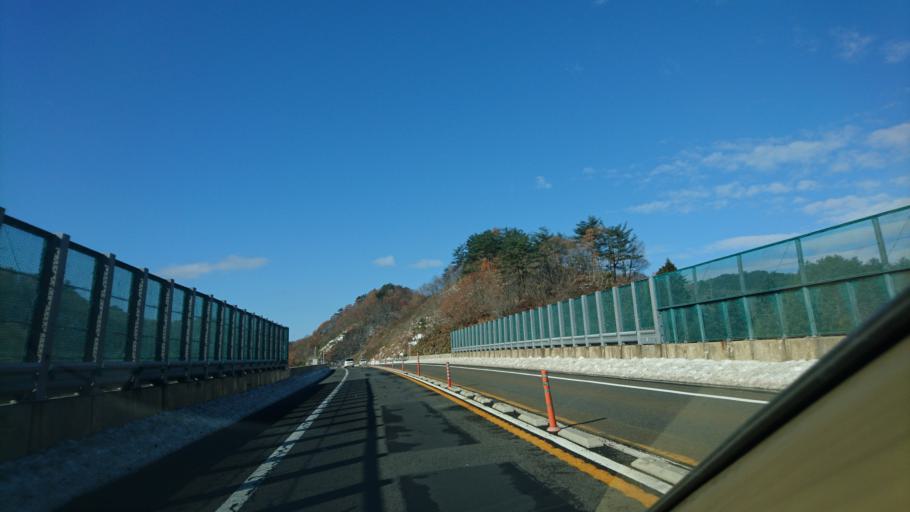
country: JP
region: Akita
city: Yokotemachi
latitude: 39.3124
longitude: 140.7730
